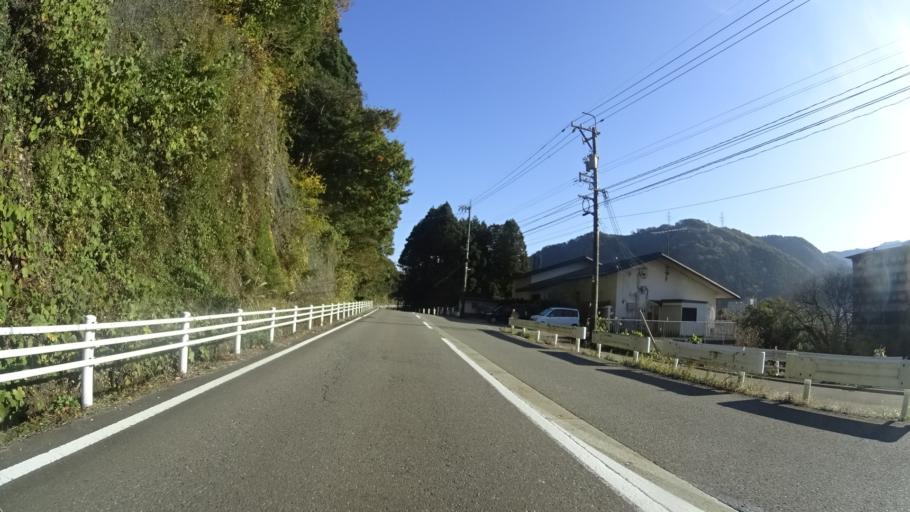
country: JP
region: Fukui
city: Maruoka
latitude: 36.2328
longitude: 136.3626
